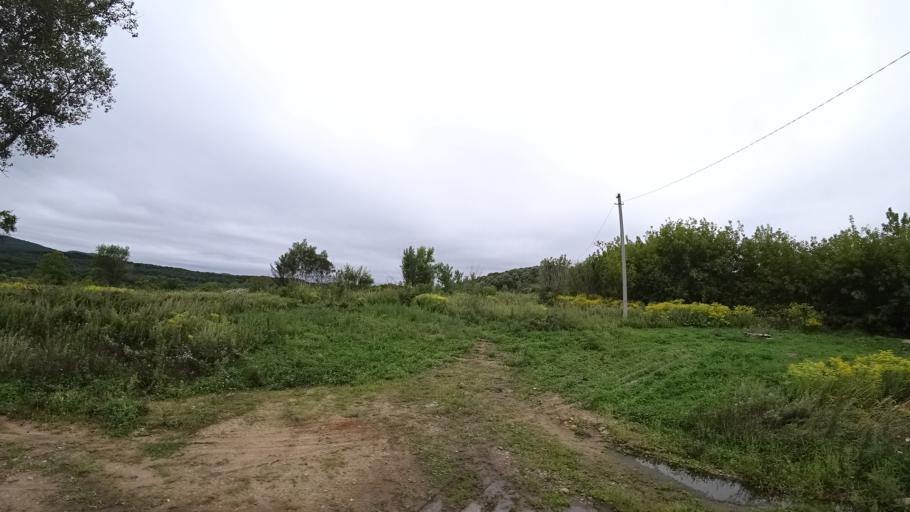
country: RU
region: Primorskiy
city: Rettikhovka
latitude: 44.1585
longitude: 132.7448
